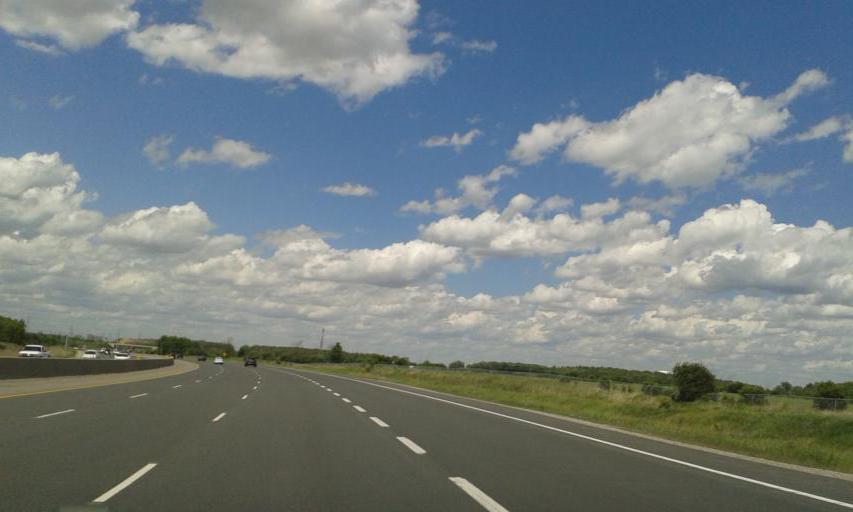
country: CA
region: Ontario
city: Oakville
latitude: 43.4883
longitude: -79.7613
